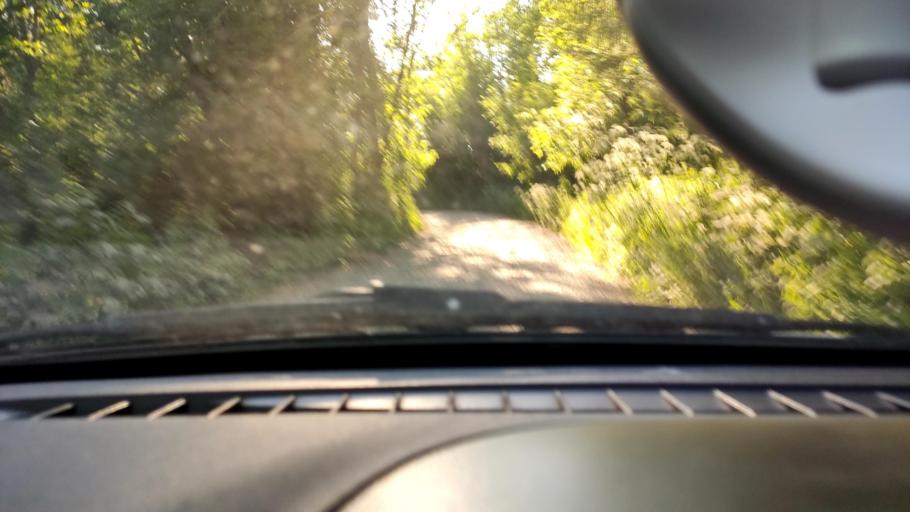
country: RU
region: Perm
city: Bershet'
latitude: 57.6967
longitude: 56.4090
